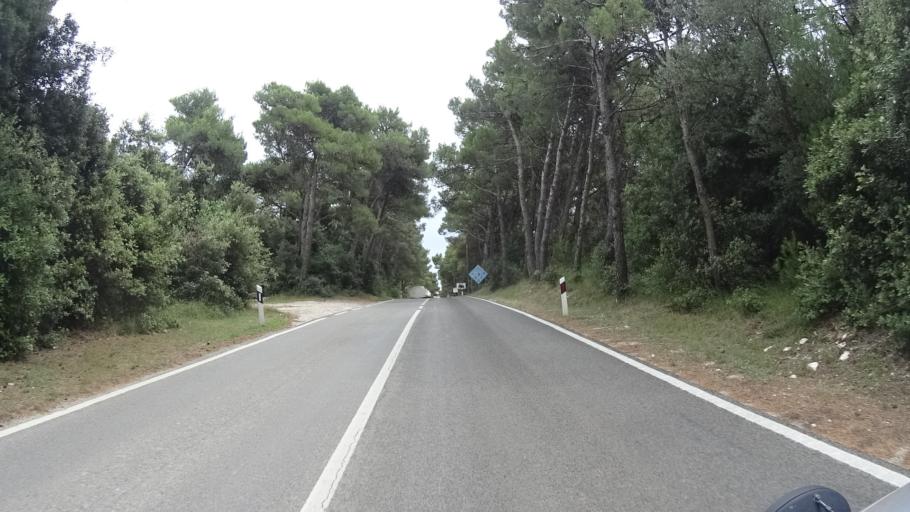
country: HR
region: Istarska
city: Medulin
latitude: 44.8089
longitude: 13.9086
